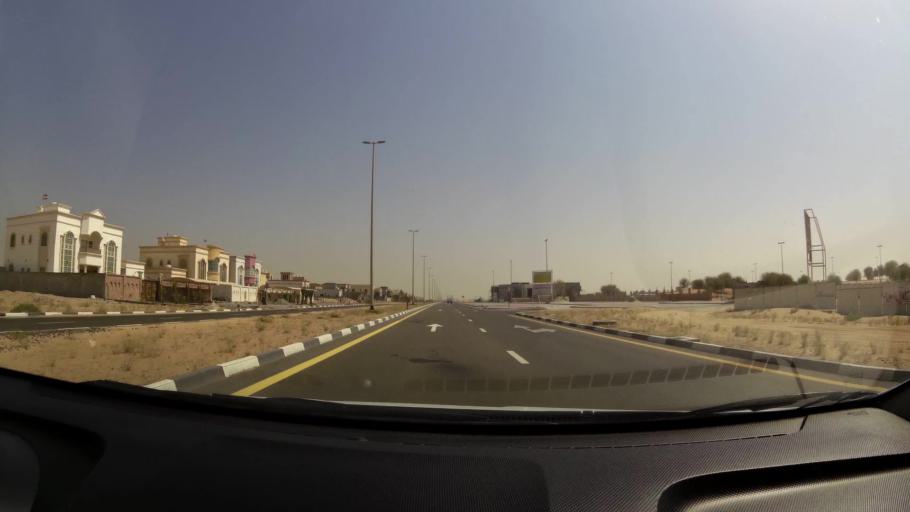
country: AE
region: Ajman
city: Ajman
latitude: 25.4024
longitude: 55.5520
